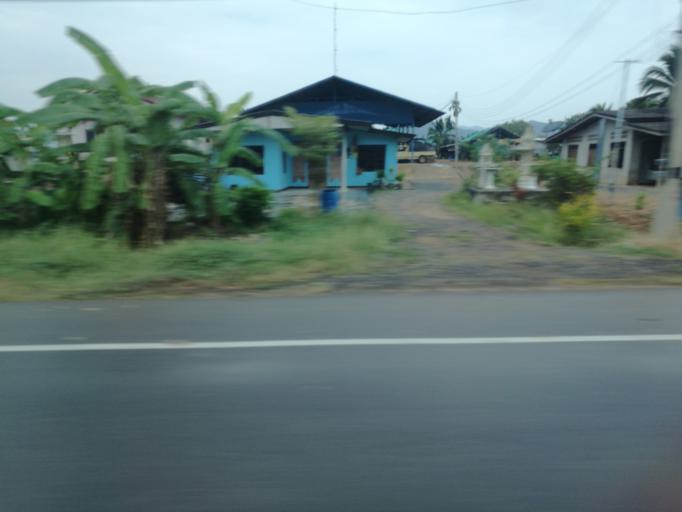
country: TH
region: Prachuap Khiri Khan
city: Kui Buri
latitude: 12.1248
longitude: 99.8526
